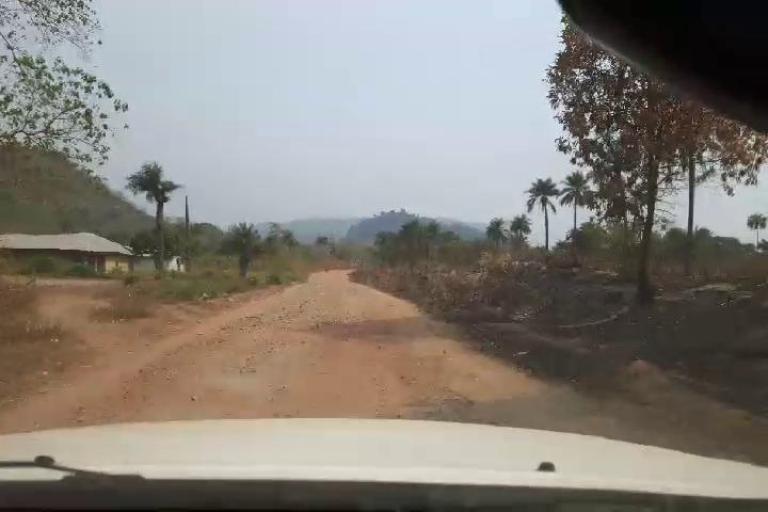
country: SL
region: Northern Province
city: Masingbi
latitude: 8.8730
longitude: -11.8181
